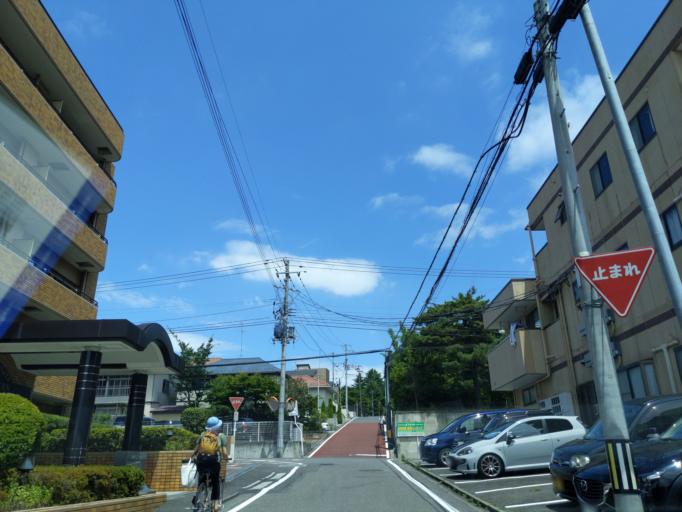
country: JP
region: Fukushima
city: Koriyama
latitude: 37.3882
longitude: 140.3764
